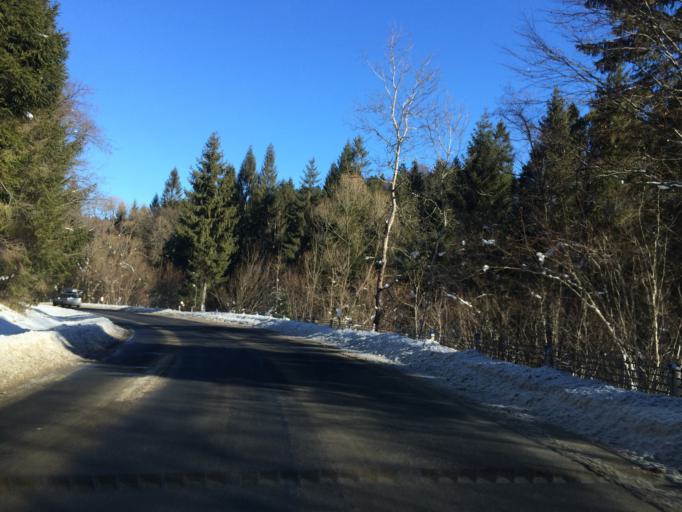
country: PL
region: Subcarpathian Voivodeship
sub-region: Powiat leski
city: Cisna
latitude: 49.2145
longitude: 22.3637
